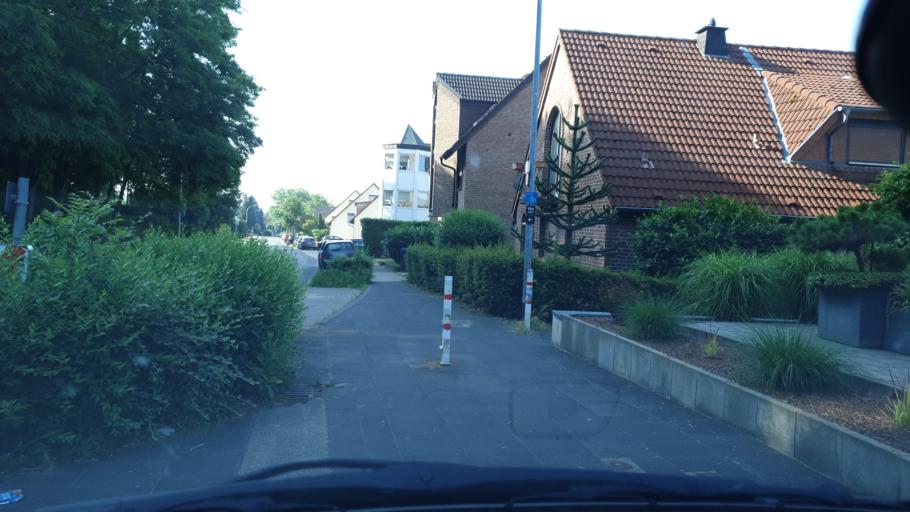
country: DE
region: North Rhine-Westphalia
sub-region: Regierungsbezirk Koln
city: Bergheim
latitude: 50.9404
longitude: 6.6932
